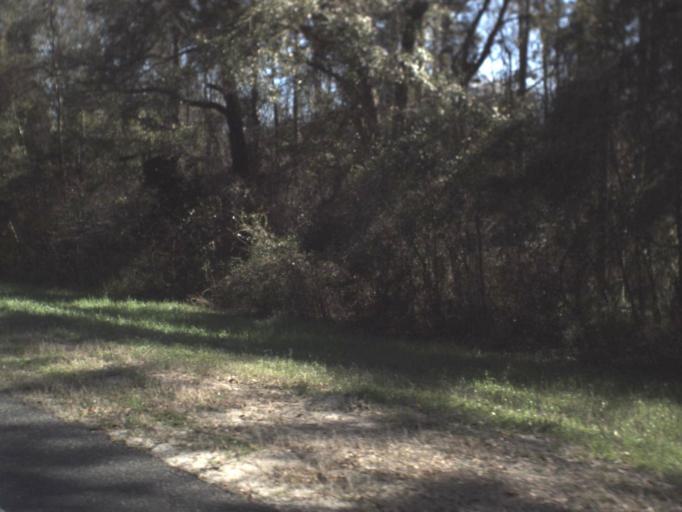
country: US
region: Florida
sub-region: Gadsden County
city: Midway
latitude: 30.4642
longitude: -84.3949
